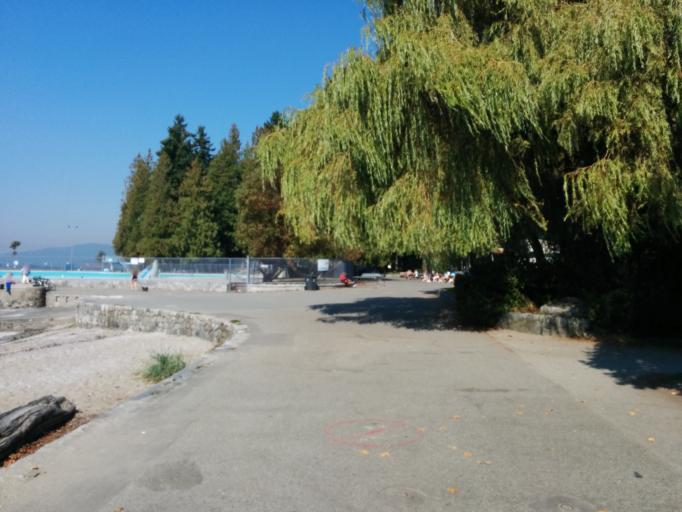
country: CA
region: British Columbia
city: West End
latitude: 49.2950
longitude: -123.1502
